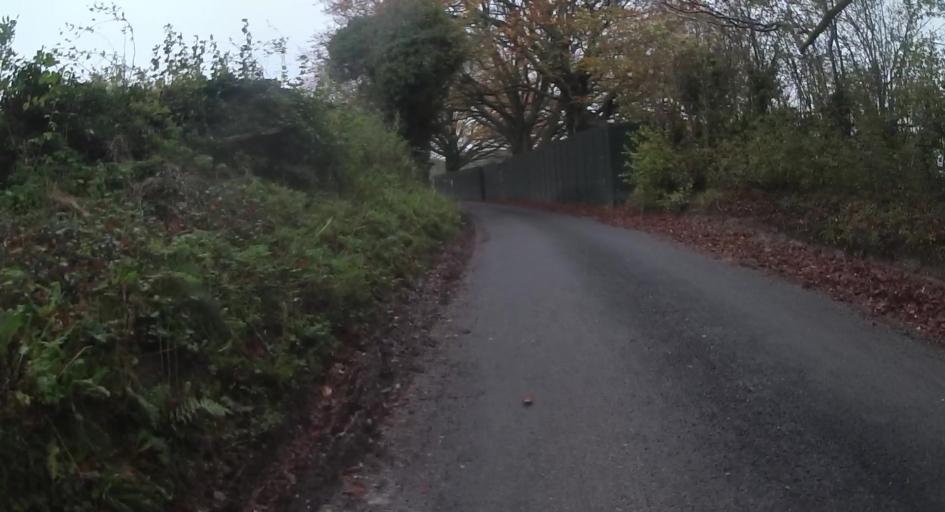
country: GB
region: England
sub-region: Hampshire
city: Four Marks
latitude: 51.1481
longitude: -1.1139
